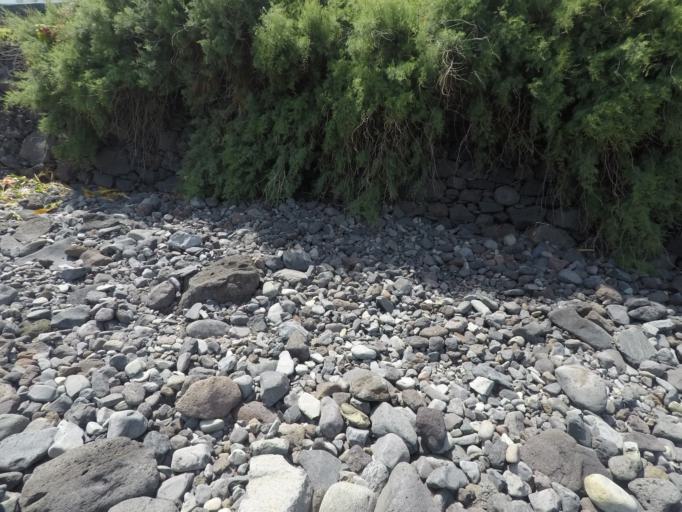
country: PT
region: Madeira
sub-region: Sao Vicente
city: Sao Vicente
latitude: 32.8294
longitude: -16.9858
